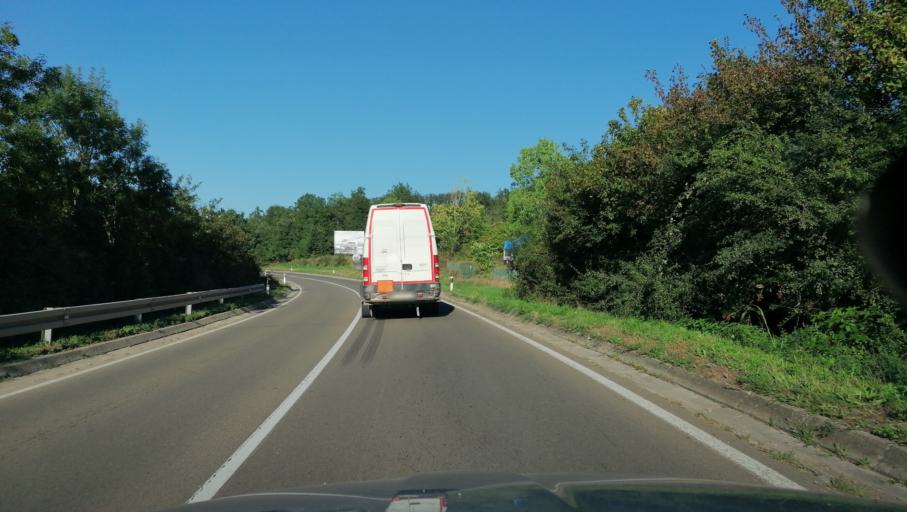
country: RS
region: Central Serbia
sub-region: Sumadijski Okrug
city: Knic
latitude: 43.9217
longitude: 20.6844
